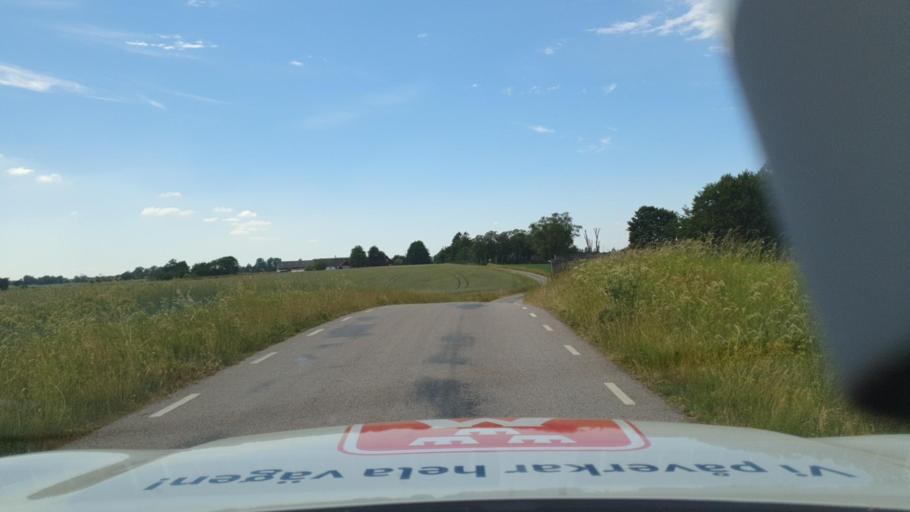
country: SE
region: Skane
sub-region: Sjobo Kommun
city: Sjoebo
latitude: 55.6309
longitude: 13.8327
